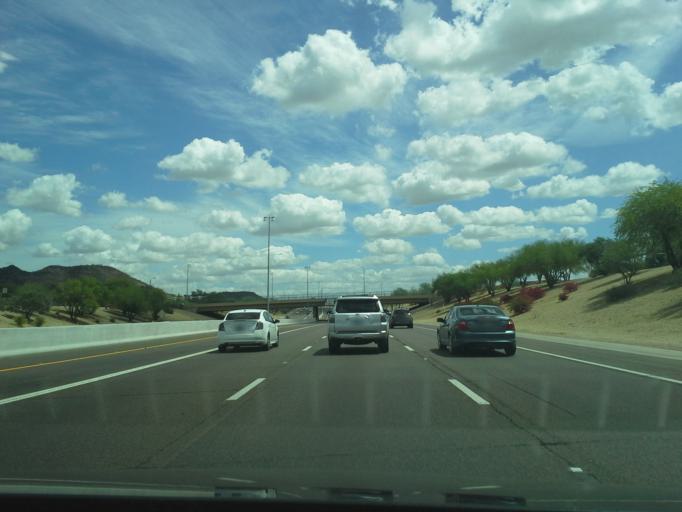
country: US
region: Arizona
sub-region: Maricopa County
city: Peoria
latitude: 33.6681
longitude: -112.1895
